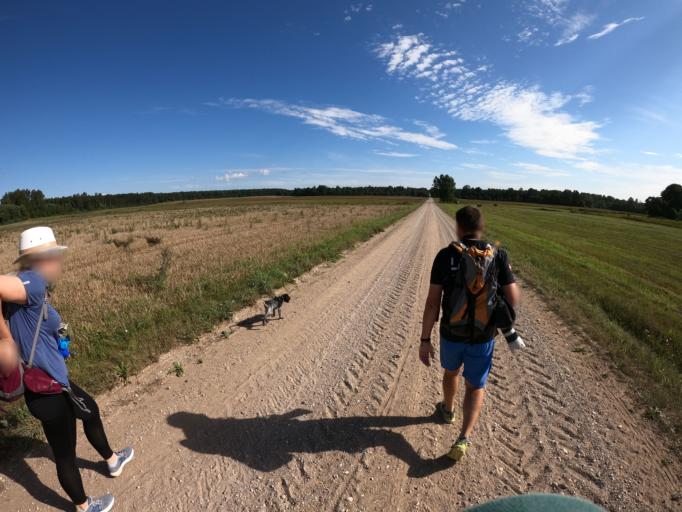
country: LV
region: Priekule
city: Priekule
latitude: 56.3724
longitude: 21.6319
